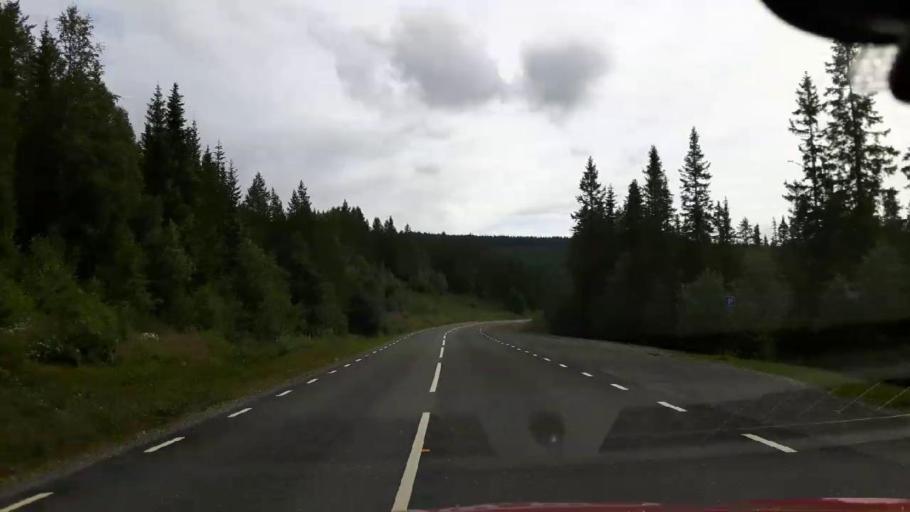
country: NO
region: Nord-Trondelag
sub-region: Lierne
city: Sandvika
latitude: 64.6361
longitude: 14.1397
